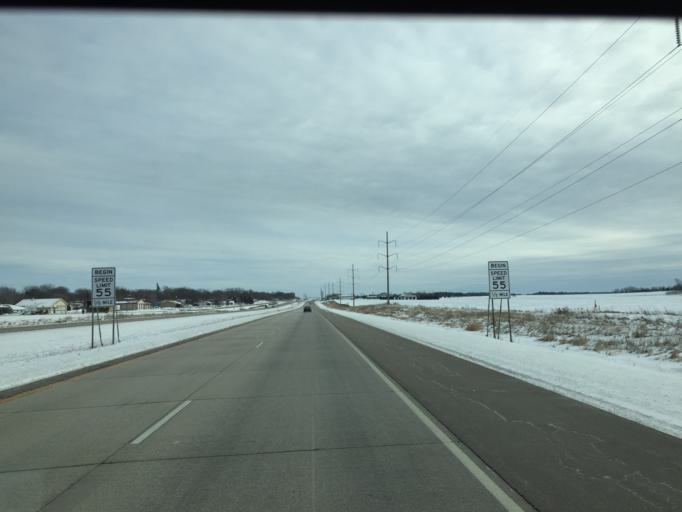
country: US
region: Minnesota
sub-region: Olmsted County
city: Byron
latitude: 44.0284
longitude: -92.6614
